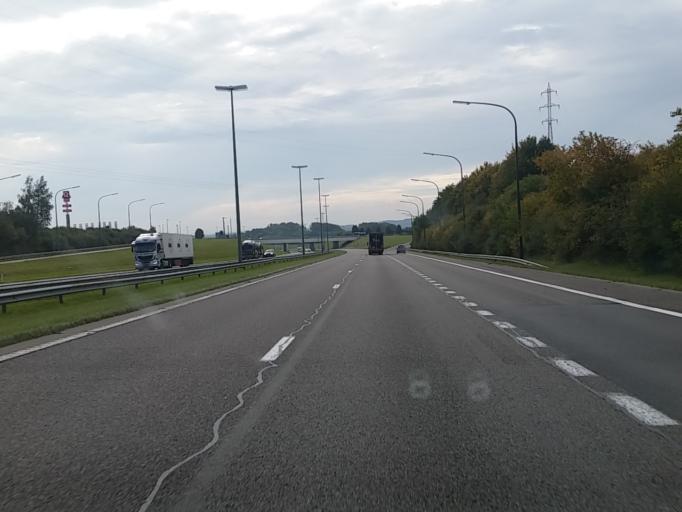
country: BE
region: Wallonia
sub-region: Province du Luxembourg
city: Arlon
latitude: 49.6555
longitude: 5.8164
